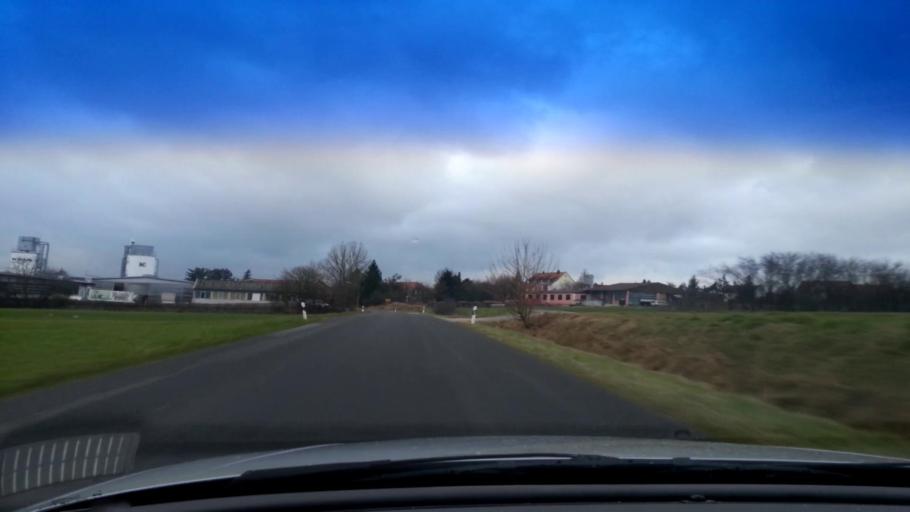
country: DE
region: Bavaria
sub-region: Upper Franconia
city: Burgebrach
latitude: 49.8359
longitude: 10.7671
